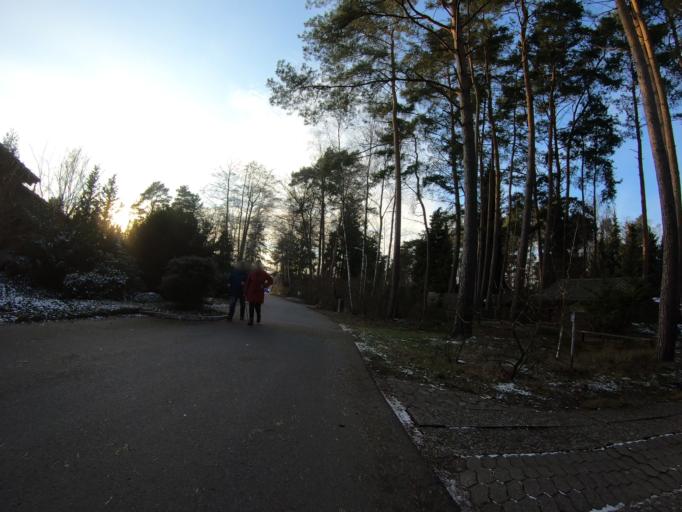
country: DE
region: Lower Saxony
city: Isenbuttel
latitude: 52.4544
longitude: 10.6118
